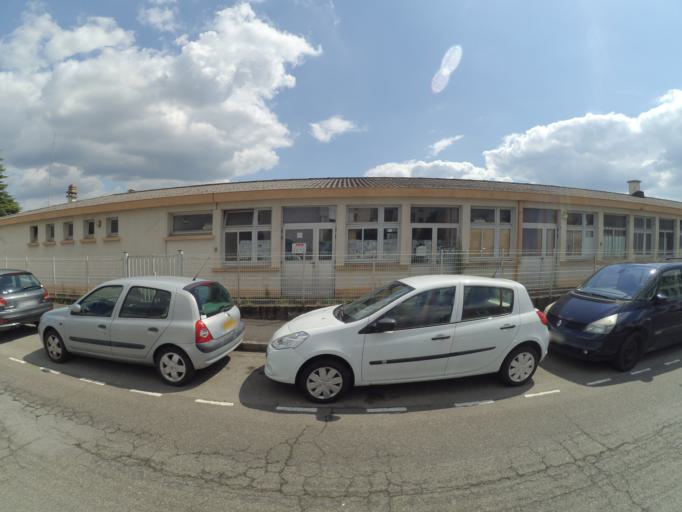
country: FR
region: Brittany
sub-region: Departement du Morbihan
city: Lorient
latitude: 47.7555
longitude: -3.3687
